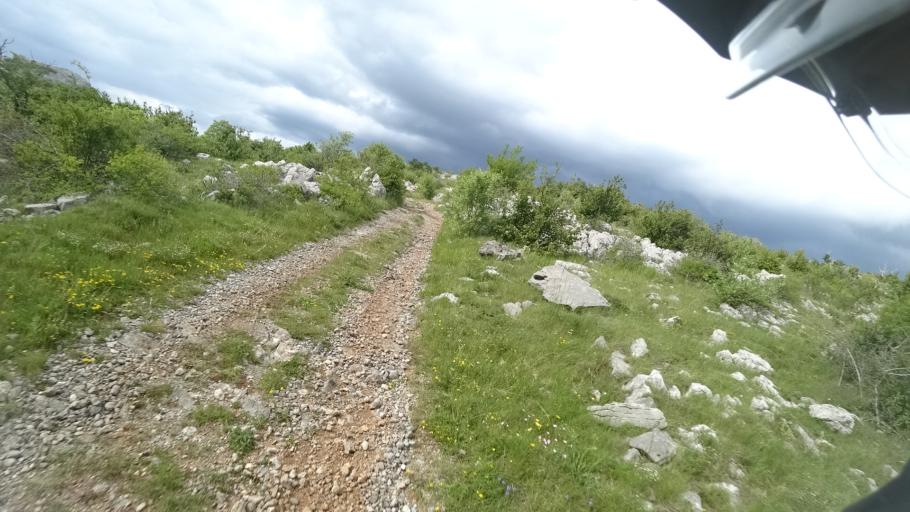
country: HR
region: Zadarska
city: Obrovac
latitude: 44.2689
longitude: 15.7395
